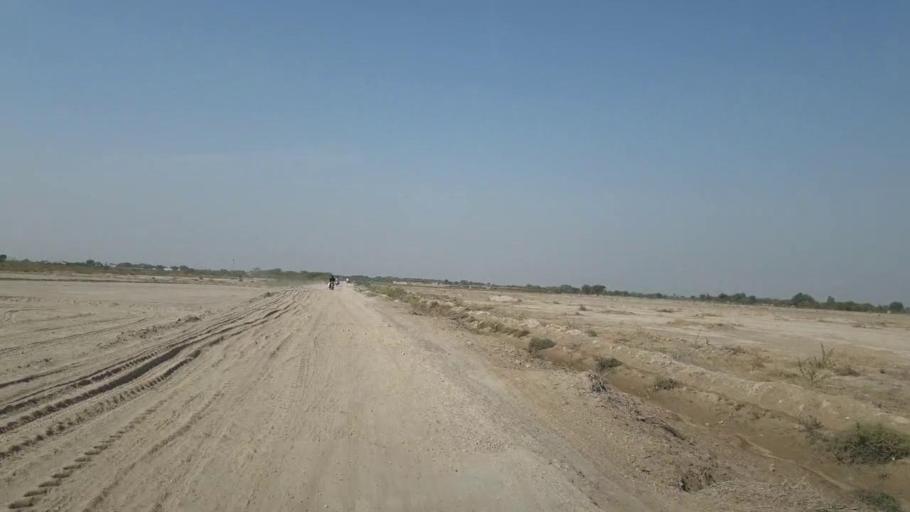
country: PK
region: Sindh
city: Nabisar
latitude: 25.0138
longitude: 69.5265
